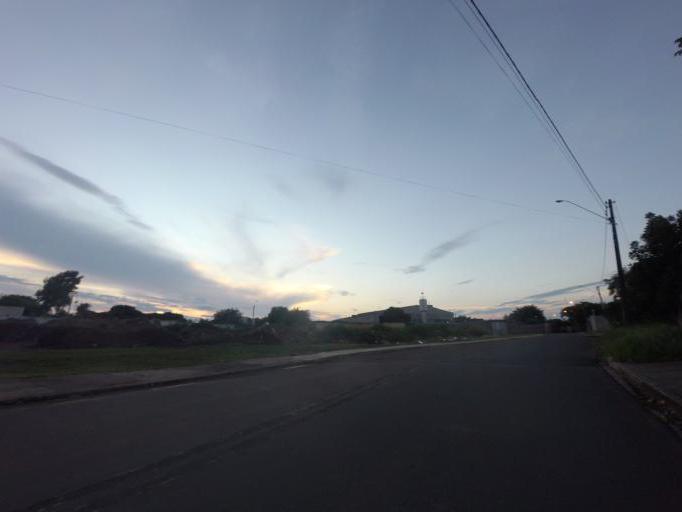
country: BR
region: Sao Paulo
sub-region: Piracicaba
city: Piracicaba
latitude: -22.7639
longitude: -47.5938
